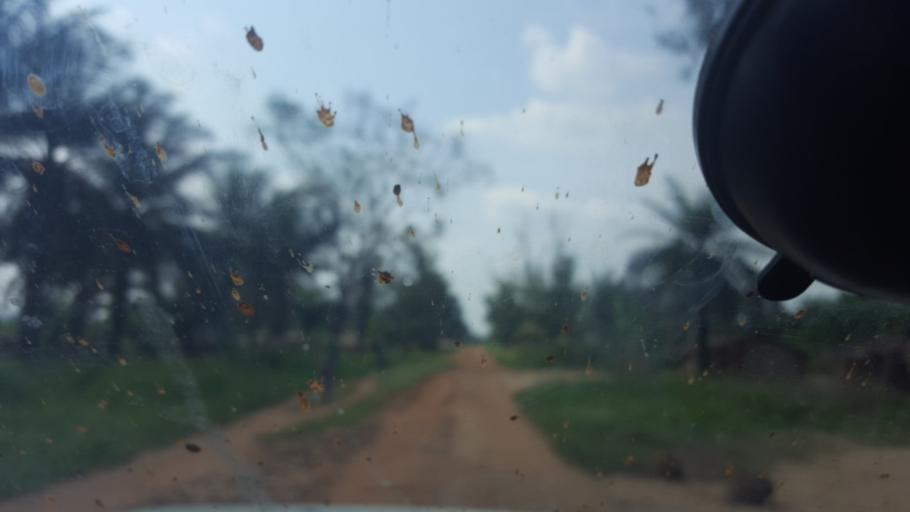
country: CD
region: Bandundu
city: Bandundu
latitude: -3.7507
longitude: 17.0385
